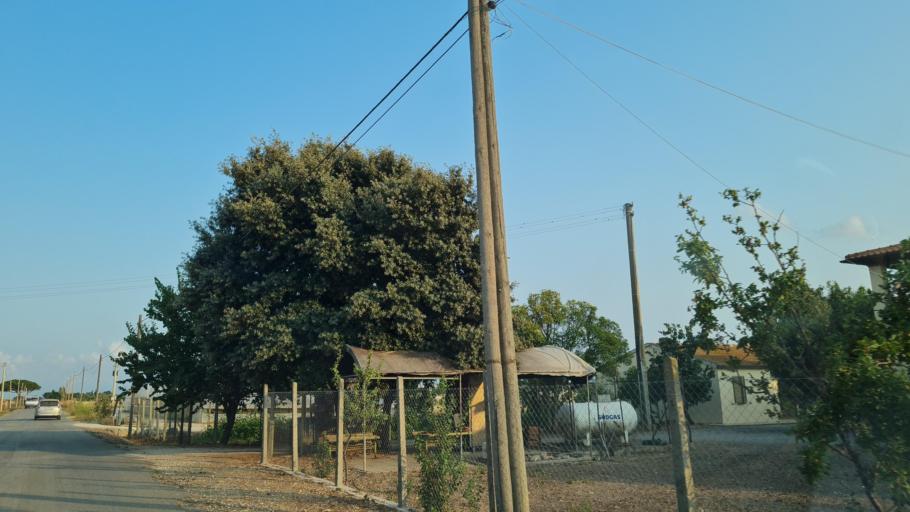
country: IT
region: Latium
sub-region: Provincia di Viterbo
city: Montalto di Castro
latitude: 42.3150
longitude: 11.6105
